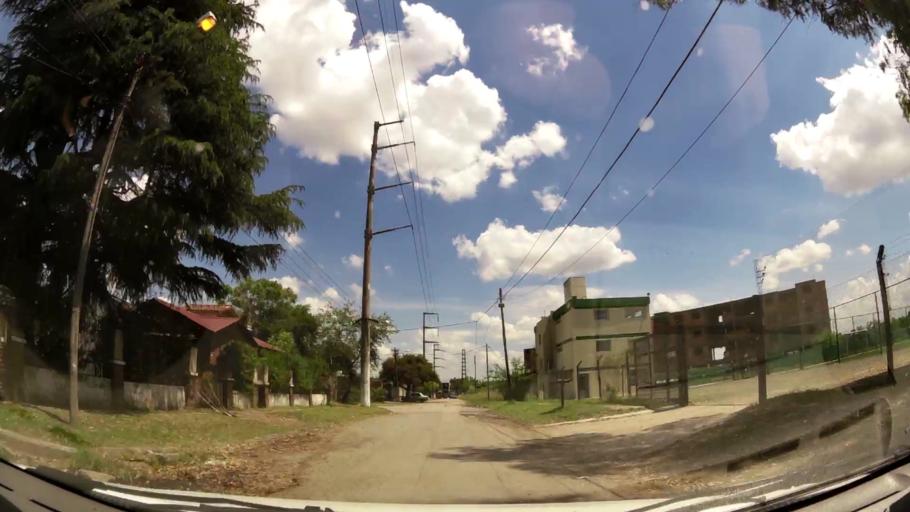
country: AR
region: Buenos Aires
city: Ituzaingo
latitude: -34.6452
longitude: -58.6878
